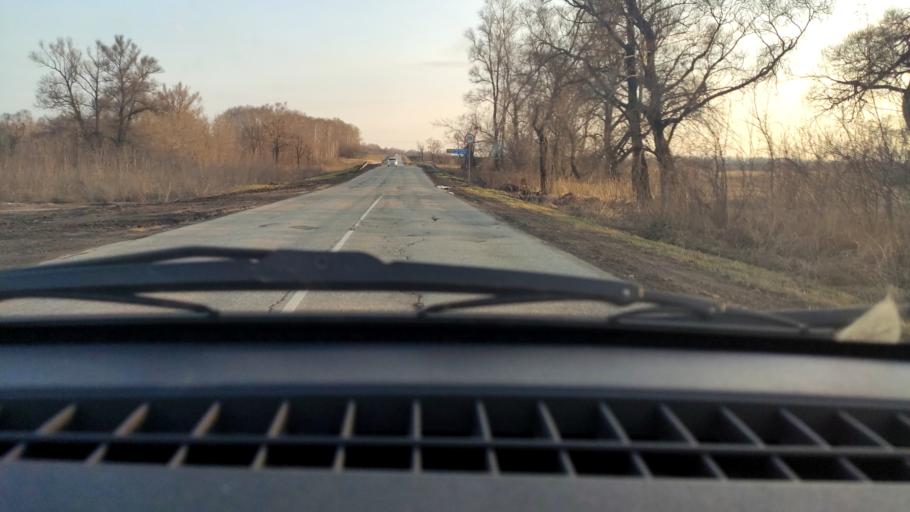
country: RU
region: Bashkortostan
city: Chishmy
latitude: 54.5140
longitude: 55.2937
